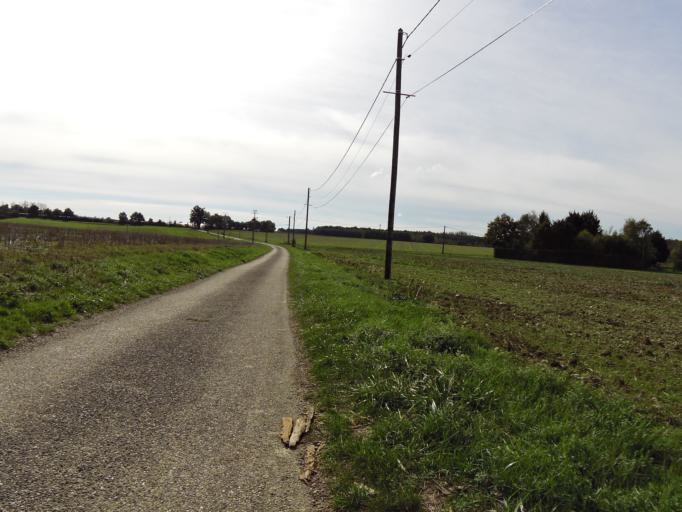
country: FR
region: Rhone-Alpes
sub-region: Departement de l'Ain
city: Perouges
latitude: 45.9411
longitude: 5.1515
